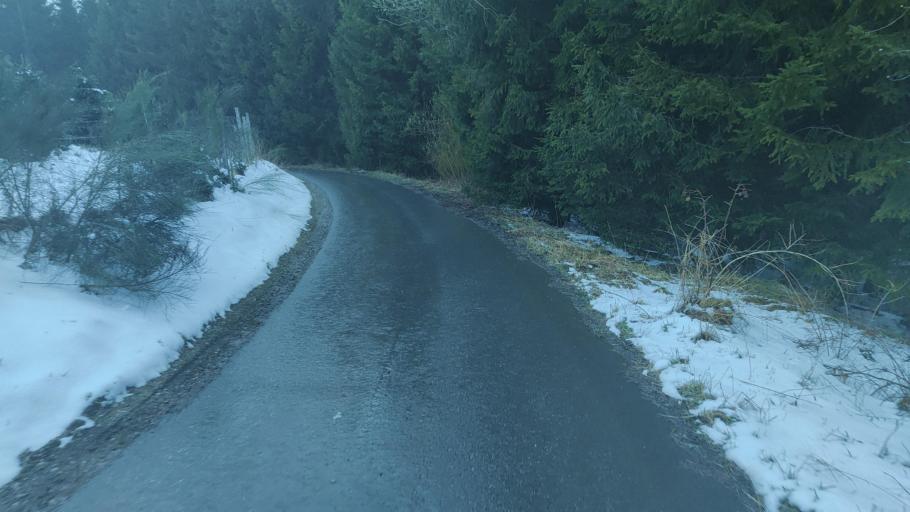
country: DE
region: North Rhine-Westphalia
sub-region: Regierungsbezirk Arnsberg
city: Bad Berleburg
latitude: 51.1559
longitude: 8.4188
